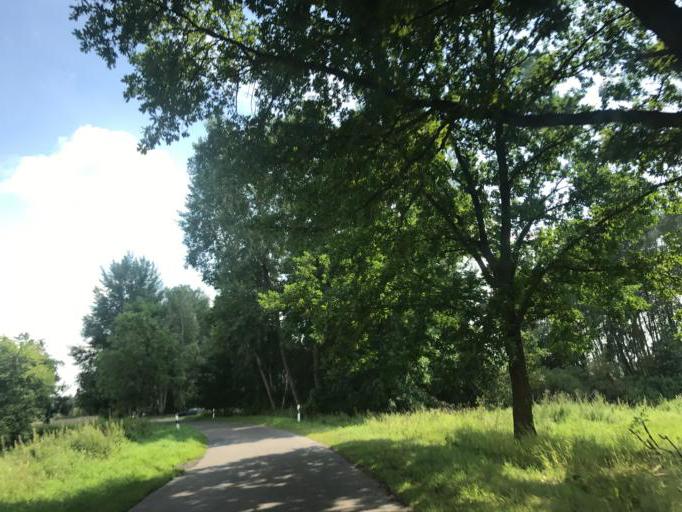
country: DE
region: Mecklenburg-Vorpommern
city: Wesenberg
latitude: 53.3127
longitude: 12.8694
